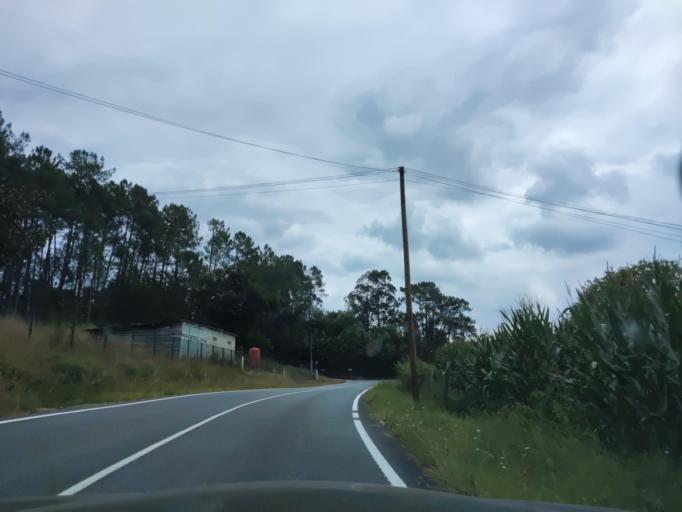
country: ES
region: Galicia
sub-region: Provincia da Coruna
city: Teo
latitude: 42.7661
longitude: -8.5551
